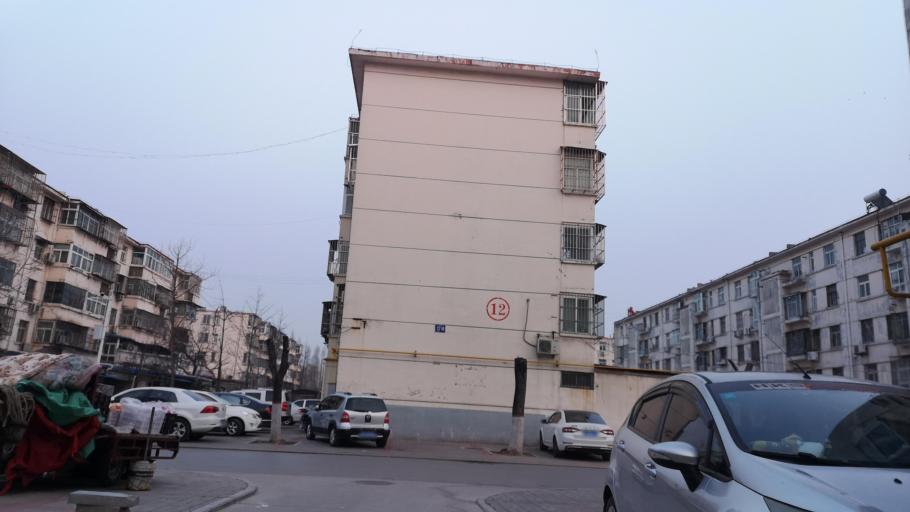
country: CN
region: Henan Sheng
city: Zhongyuanlu
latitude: 35.7817
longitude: 115.0747
